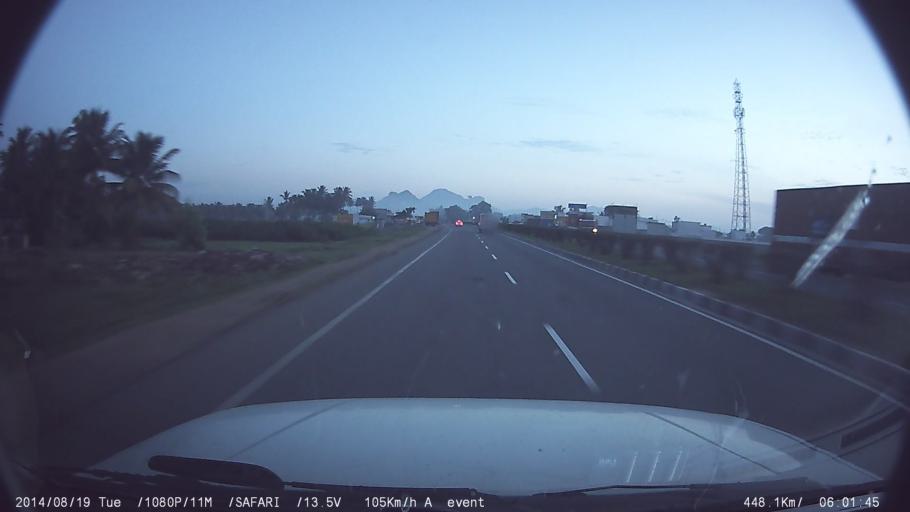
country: IN
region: Tamil Nadu
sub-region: Salem
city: Omalur
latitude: 11.8266
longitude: 78.0663
